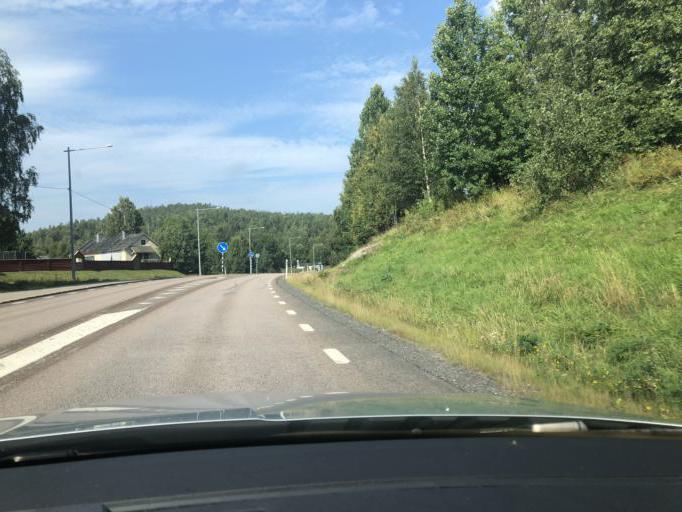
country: SE
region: Vaesternorrland
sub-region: Kramfors Kommun
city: Kramfors
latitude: 62.8029
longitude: 17.8688
